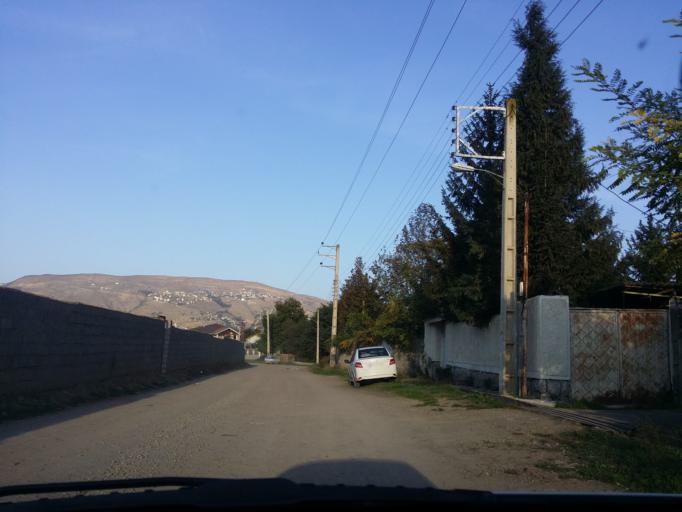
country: IR
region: Mazandaran
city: `Abbasabad
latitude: 36.5093
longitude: 51.1865
